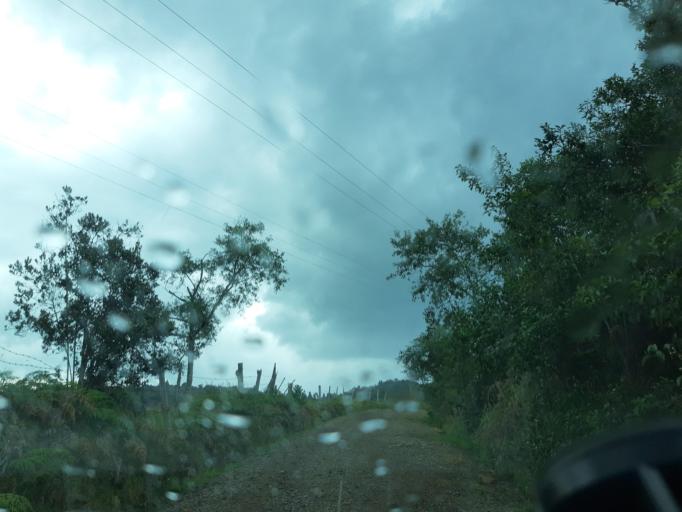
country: CO
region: Boyaca
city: Raquira
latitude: 5.4944
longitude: -73.6946
